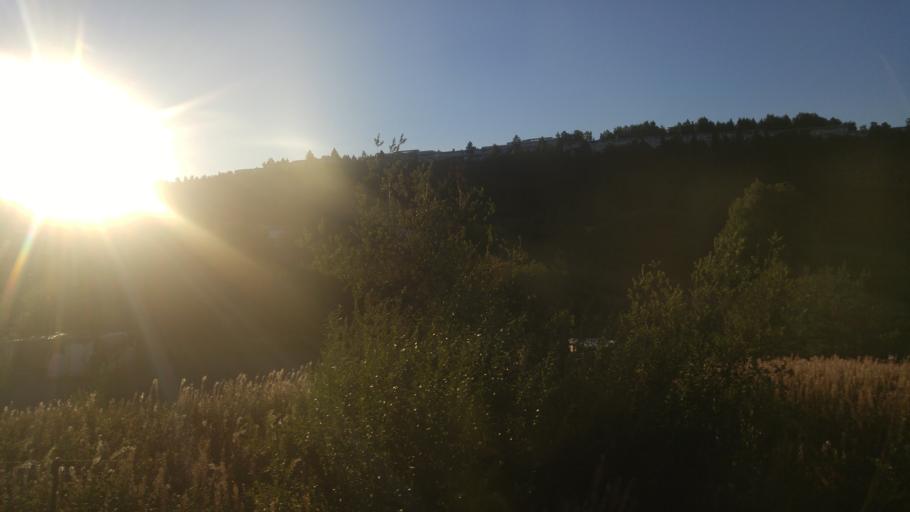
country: NO
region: Oslo
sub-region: Oslo
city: Oslo
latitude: 59.9191
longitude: 10.8310
